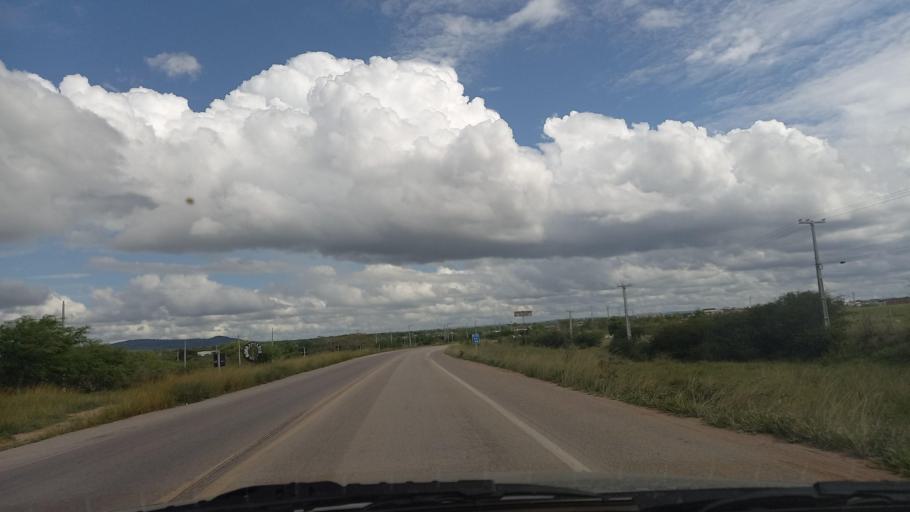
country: BR
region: Pernambuco
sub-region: Cachoeirinha
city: Cachoeirinha
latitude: -8.4821
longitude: -36.2250
